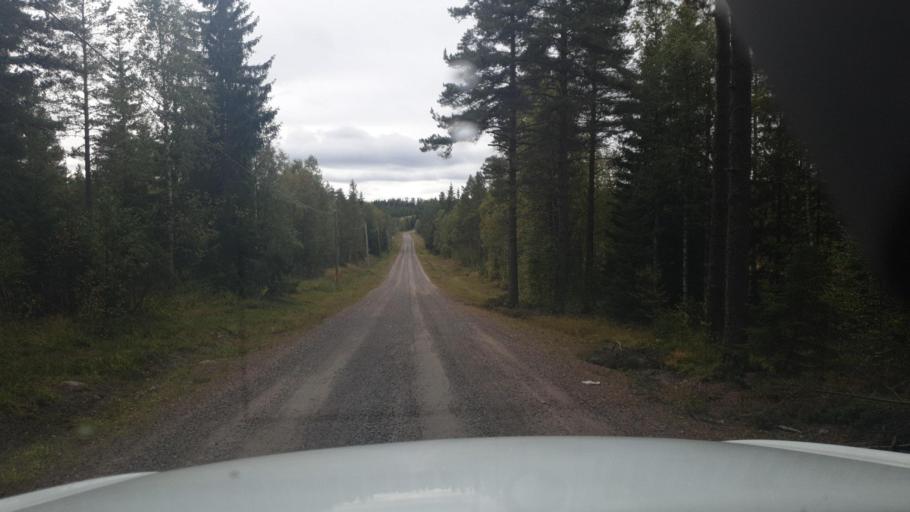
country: SE
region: Vaermland
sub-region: Torsby Kommun
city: Torsby
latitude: 60.1677
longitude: 12.6211
